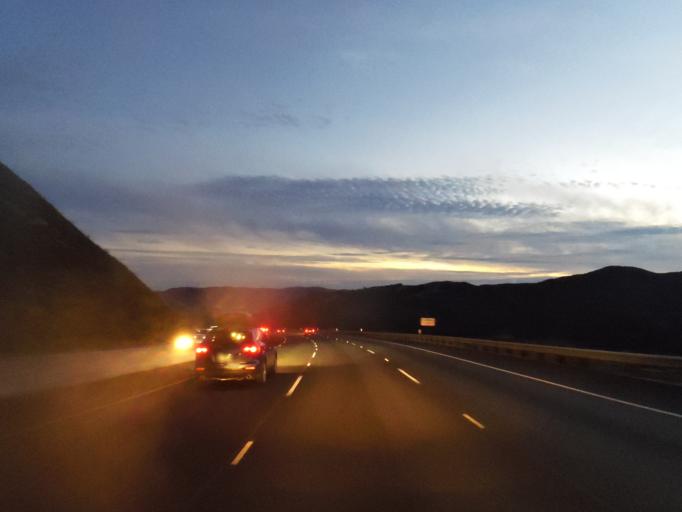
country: US
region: California
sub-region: San Luis Obispo County
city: Santa Margarita
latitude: 35.3405
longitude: -120.6278
